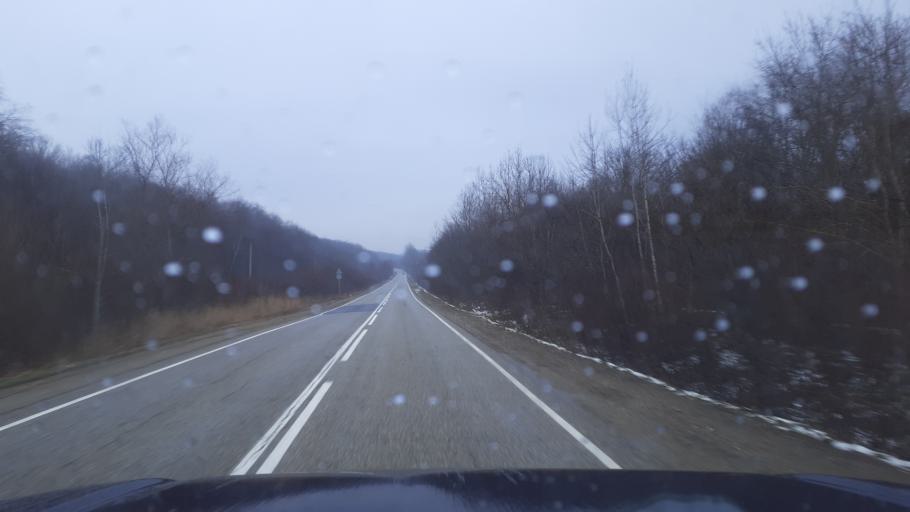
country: RU
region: Krasnodarskiy
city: Neftegorsk
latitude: 44.2772
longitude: 39.7928
